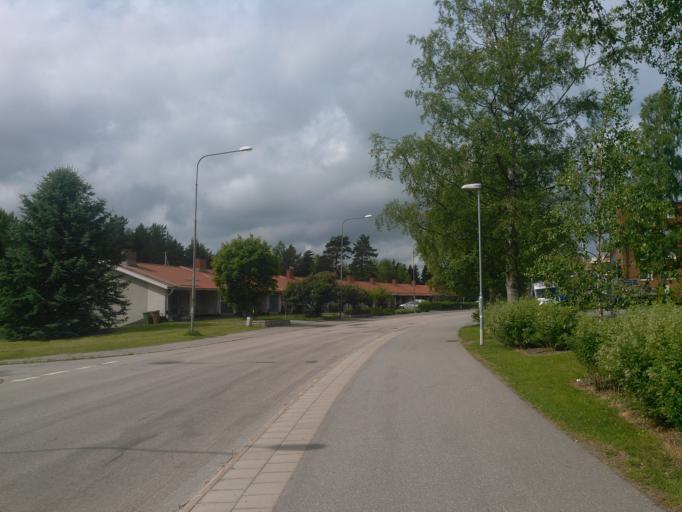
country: SE
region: Vaesterbotten
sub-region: Umea Kommun
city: Umea
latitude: 63.8238
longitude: 20.2974
